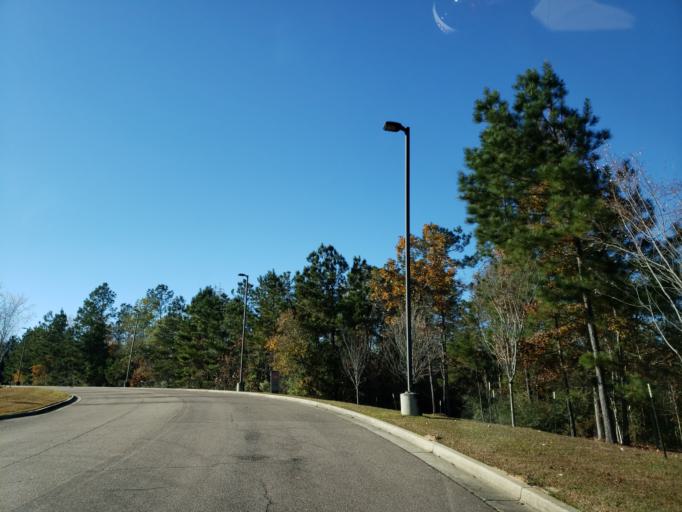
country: US
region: Mississippi
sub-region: Forrest County
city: Hattiesburg
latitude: 31.2825
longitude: -89.3276
